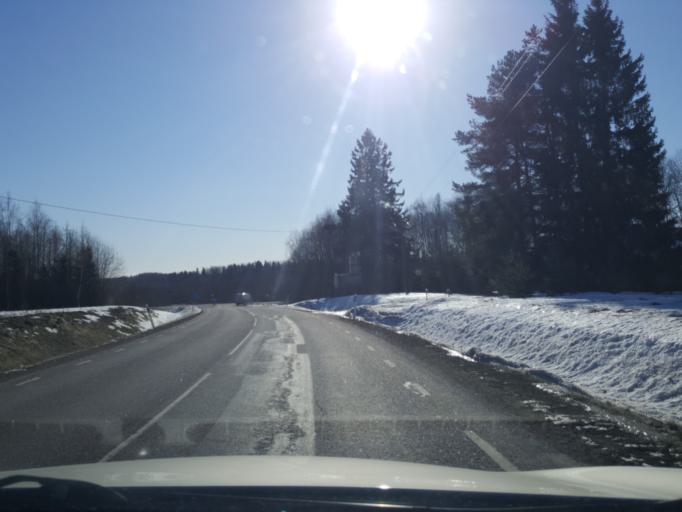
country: EE
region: Viljandimaa
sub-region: Viiratsi vald
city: Viiratsi
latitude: 58.4089
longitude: 25.6664
